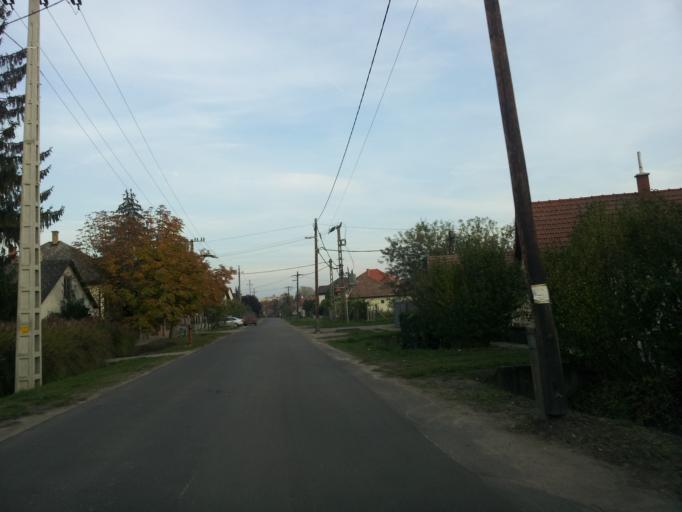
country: HU
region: Pest
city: Nagykata
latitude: 47.4182
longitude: 19.7332
